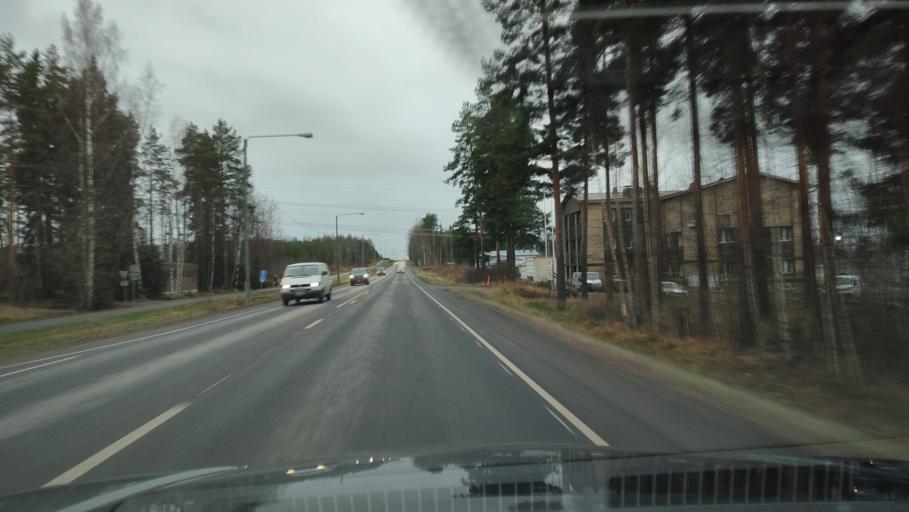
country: FI
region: Southern Ostrobothnia
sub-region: Seinaejoki
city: Seinaejoki
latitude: 62.7849
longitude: 22.7143
